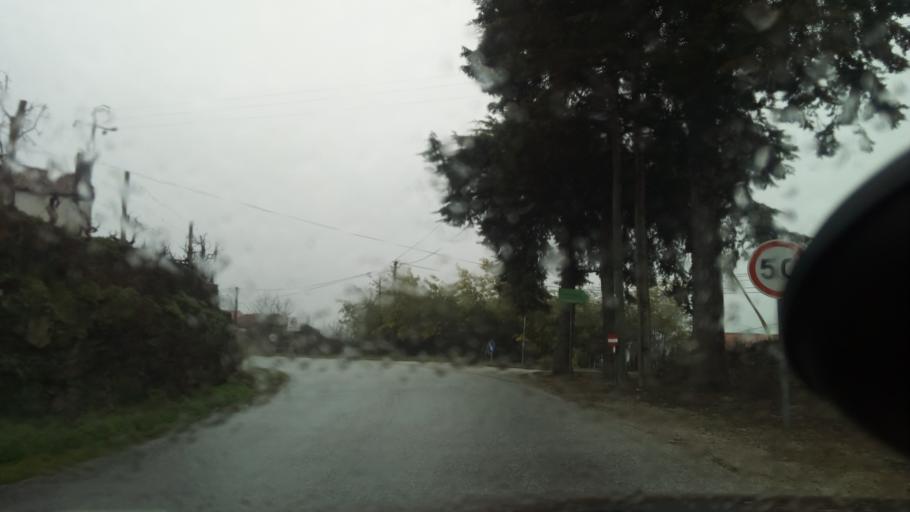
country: PT
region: Viseu
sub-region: Mangualde
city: Mangualde
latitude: 40.6117
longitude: -7.6748
